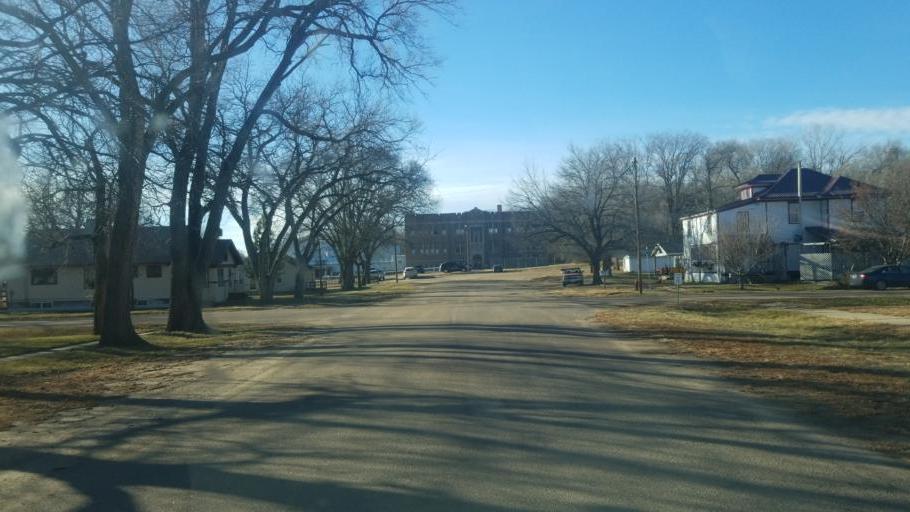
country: US
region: South Dakota
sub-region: Charles Mix County
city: Wagner
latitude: 42.8303
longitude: -98.4692
